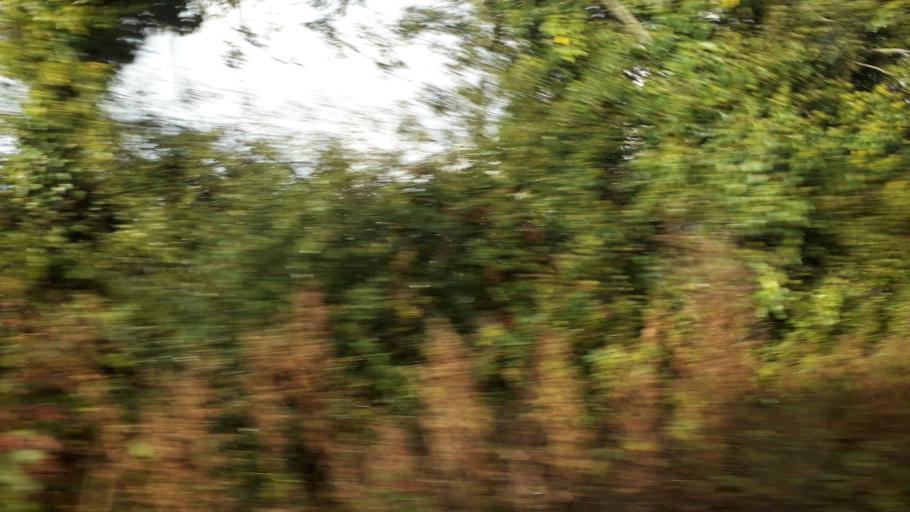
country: IE
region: Connaught
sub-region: Roscommon
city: Roscommon
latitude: 53.7738
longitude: -8.1258
